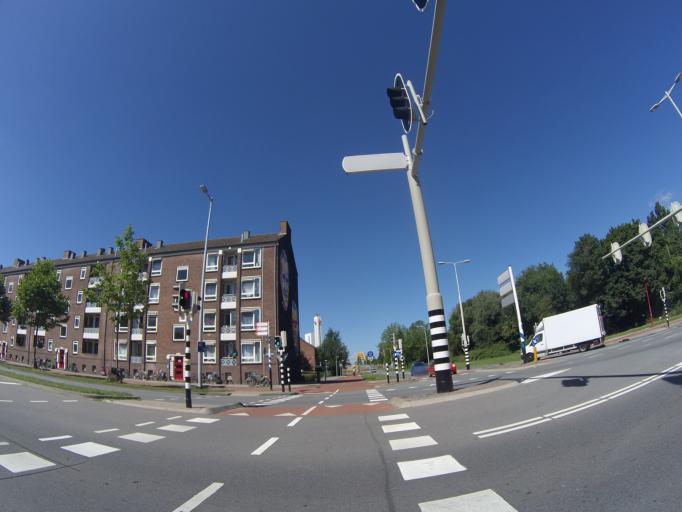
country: NL
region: Utrecht
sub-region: Gemeente Utrecht
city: Utrecht
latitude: 52.0970
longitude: 5.0860
